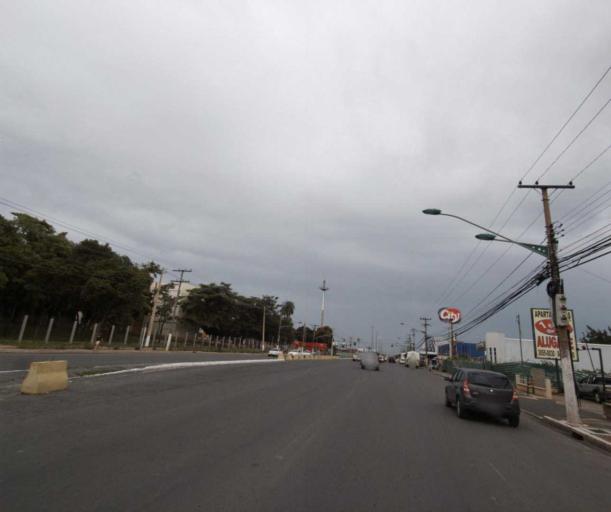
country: BR
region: Mato Grosso
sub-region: Cuiaba
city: Cuiaba
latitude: -15.6153
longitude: -56.0723
